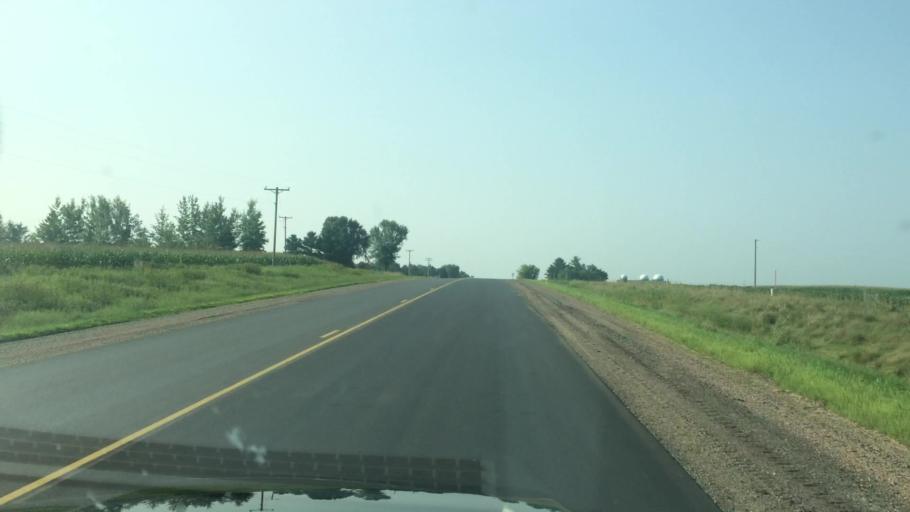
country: US
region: Wisconsin
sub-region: Marathon County
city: Stratford
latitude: 44.8747
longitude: -90.0790
